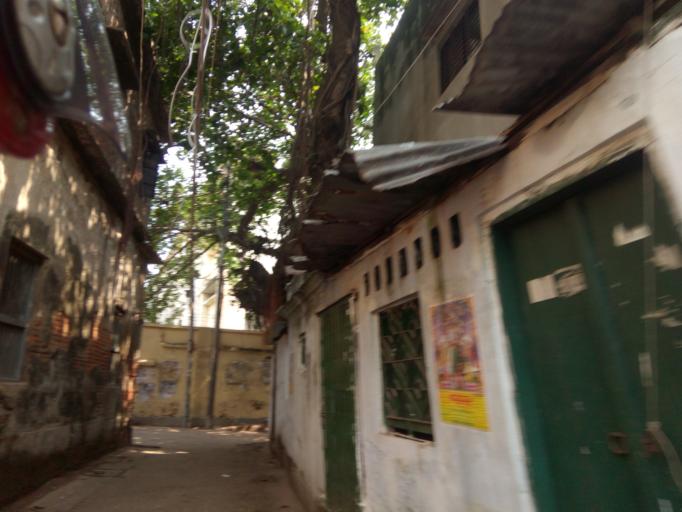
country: BD
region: Dhaka
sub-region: Dhaka
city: Dhaka
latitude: 23.7007
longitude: 90.4190
